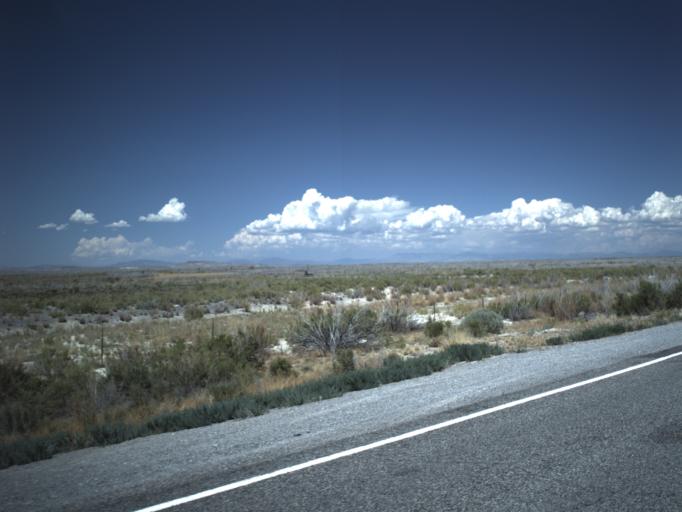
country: US
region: Utah
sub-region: Millard County
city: Delta
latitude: 39.2585
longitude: -112.8834
